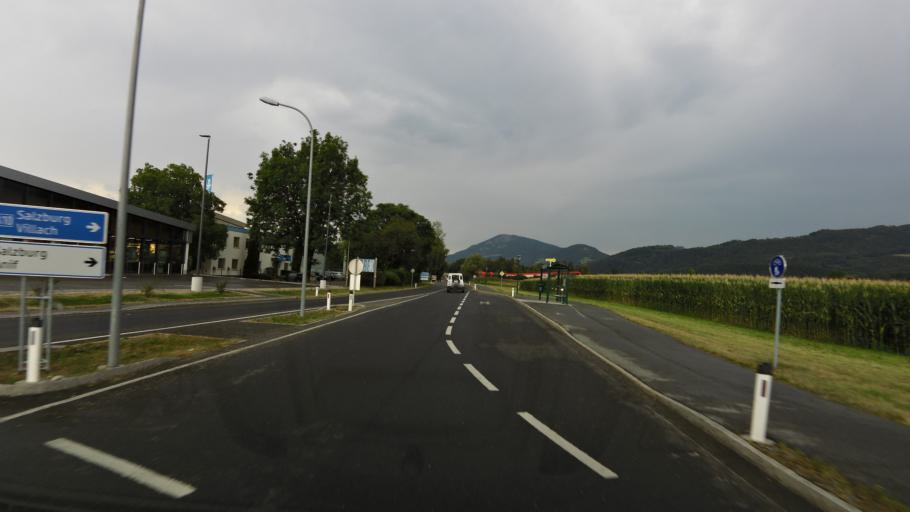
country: AT
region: Salzburg
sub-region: Politischer Bezirk Salzburg-Umgebung
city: Anif
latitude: 47.7330
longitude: 13.0655
